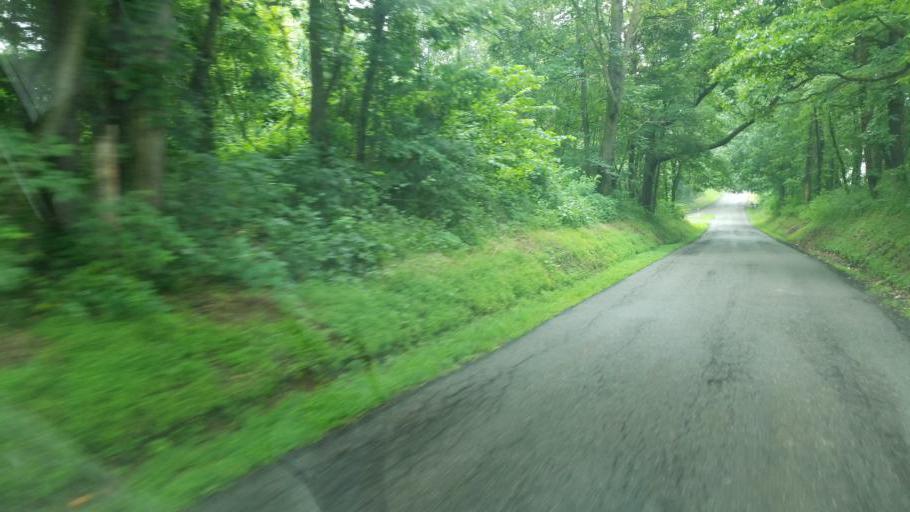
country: US
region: Ohio
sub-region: Columbiana County
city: Salineville
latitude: 40.5556
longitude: -80.8383
